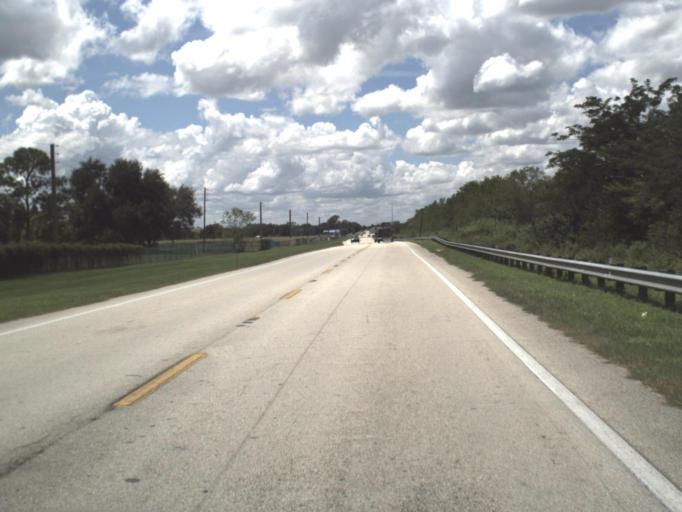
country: US
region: Florida
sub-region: Polk County
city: Dundee
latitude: 28.0188
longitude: -81.6455
